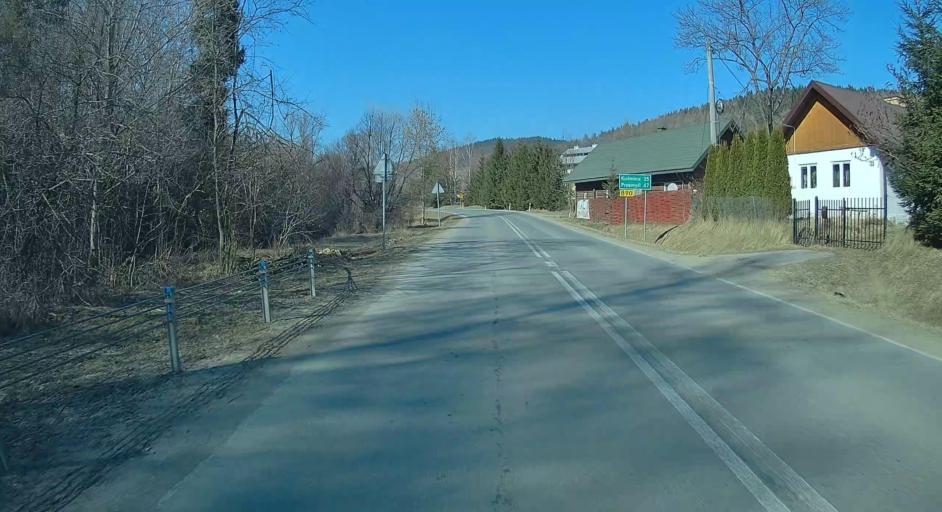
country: PL
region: Subcarpathian Voivodeship
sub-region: Powiat bieszczadzki
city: Ustrzyki Dolne
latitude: 49.4793
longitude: 22.6674
